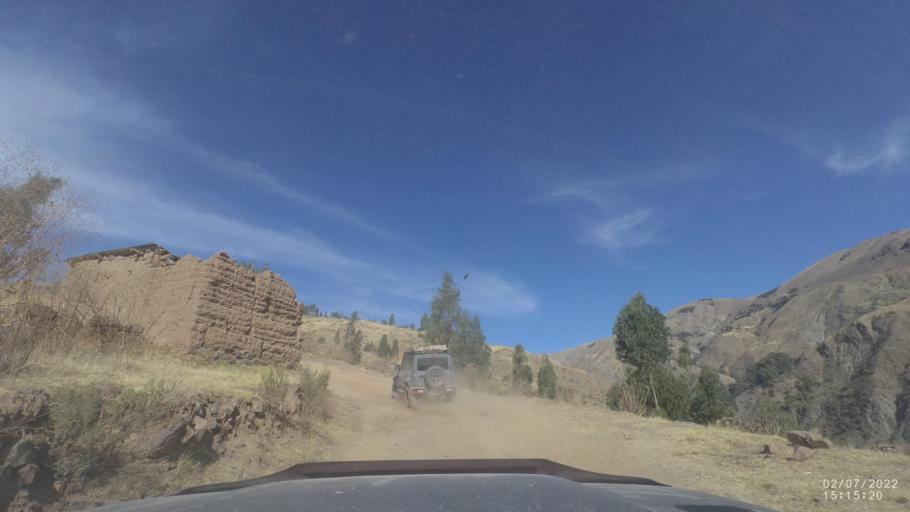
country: BO
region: Cochabamba
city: Irpa Irpa
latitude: -17.8641
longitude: -66.4352
